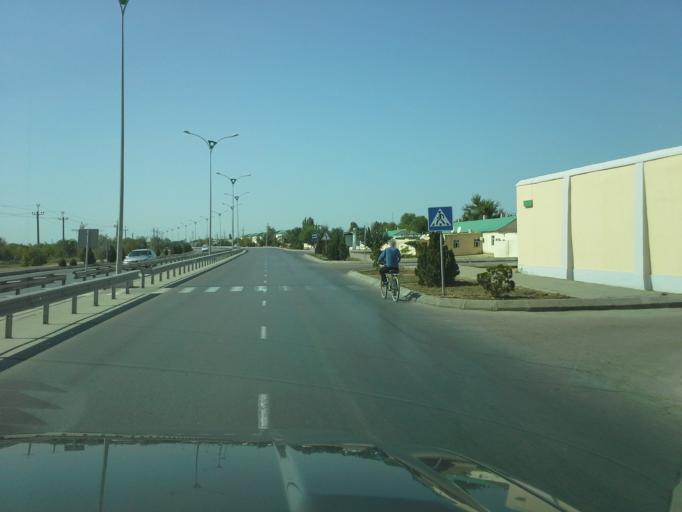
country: TM
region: Dasoguz
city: Dasoguz
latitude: 41.8492
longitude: 59.9287
